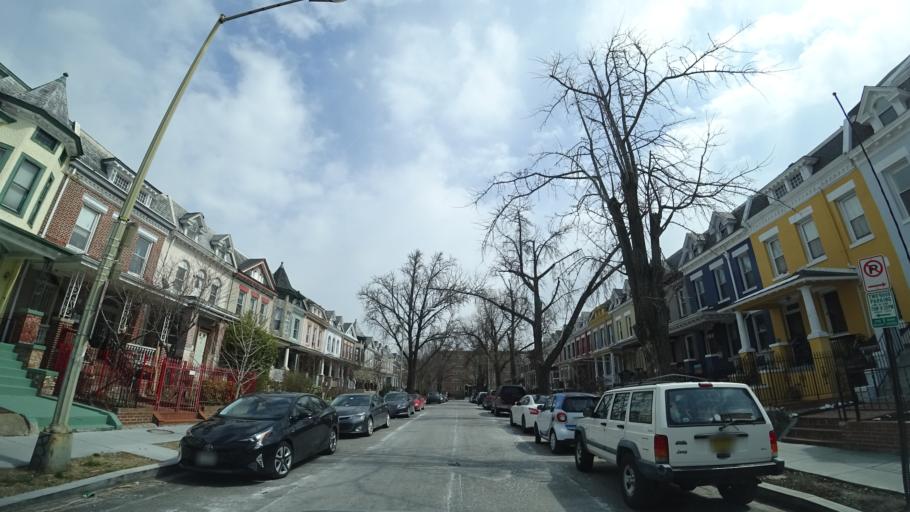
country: US
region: Washington, D.C.
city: Washington, D.C.
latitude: 38.9332
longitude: -77.0324
